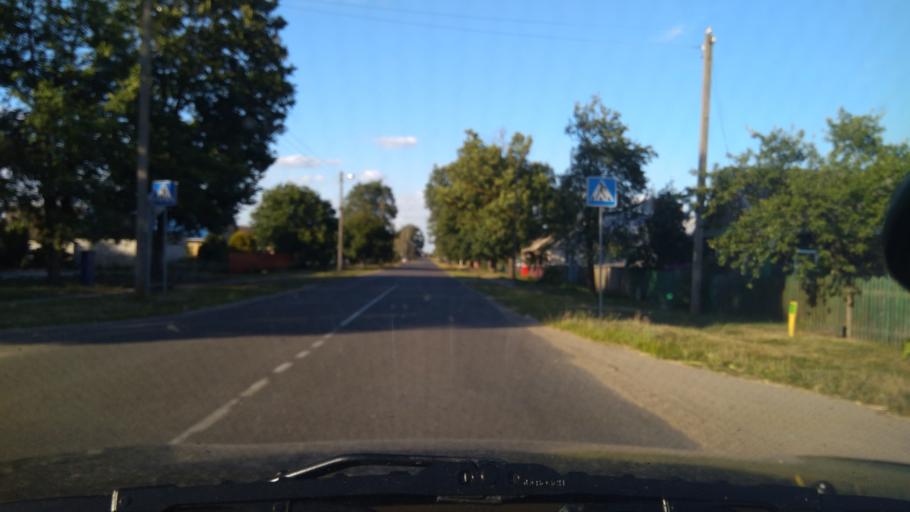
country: BY
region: Brest
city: Byaroza
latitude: 52.5850
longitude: 24.8650
